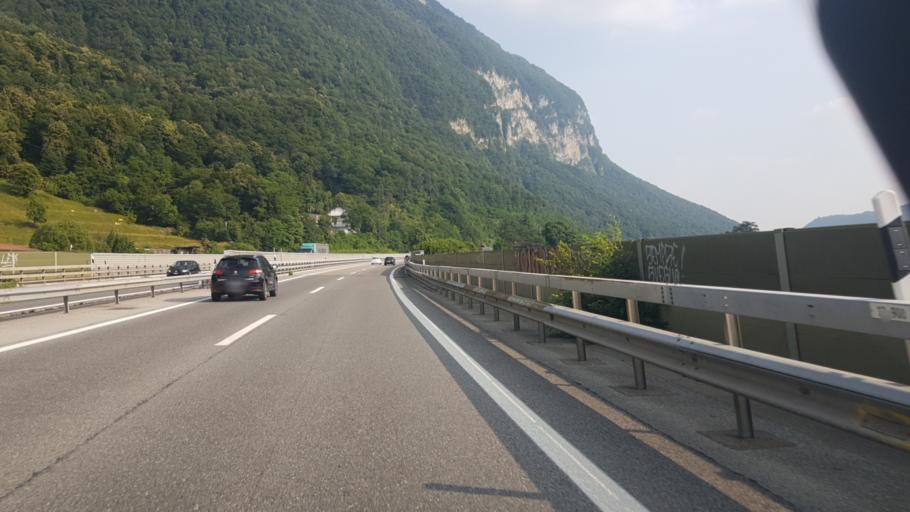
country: CH
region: Ticino
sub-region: Lugano District
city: Melano
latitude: 45.9185
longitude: 8.9846
